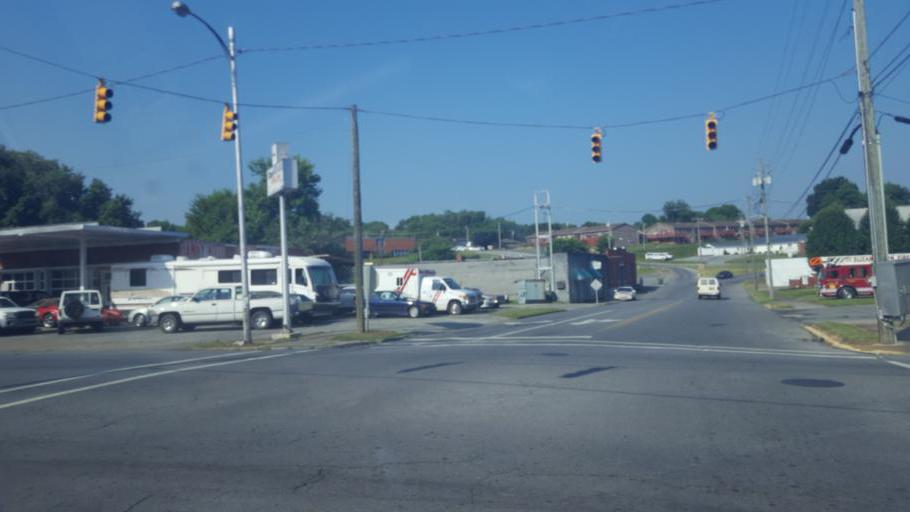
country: US
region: Tennessee
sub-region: Carter County
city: Elizabethton
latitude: 36.3468
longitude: -82.2141
